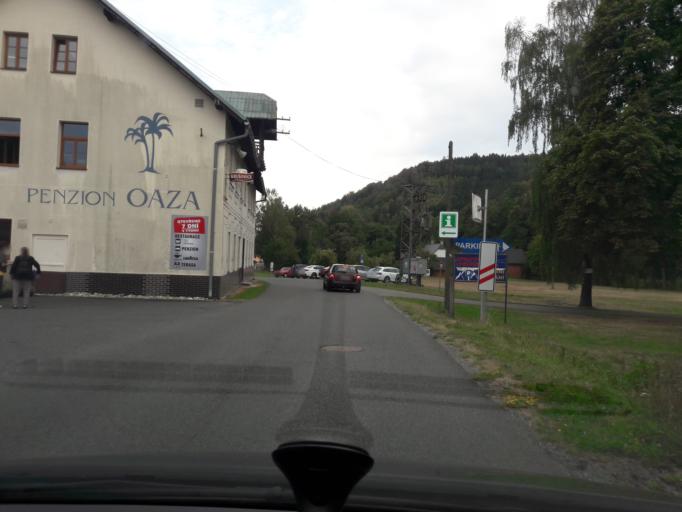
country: CZ
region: Olomoucky
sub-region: Okres Sumperk
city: Loucna nad Desnou
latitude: 50.0748
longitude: 17.0869
